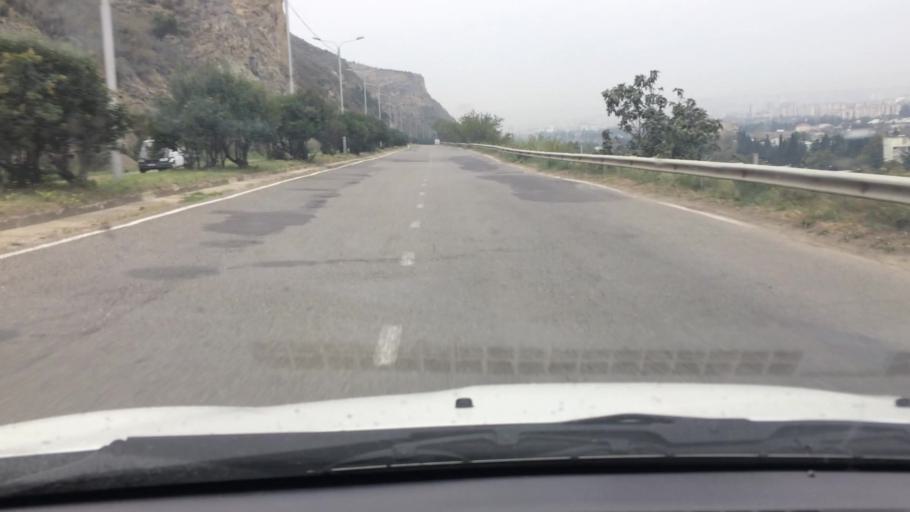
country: GE
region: T'bilisi
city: Tbilisi
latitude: 41.6530
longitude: 44.9019
